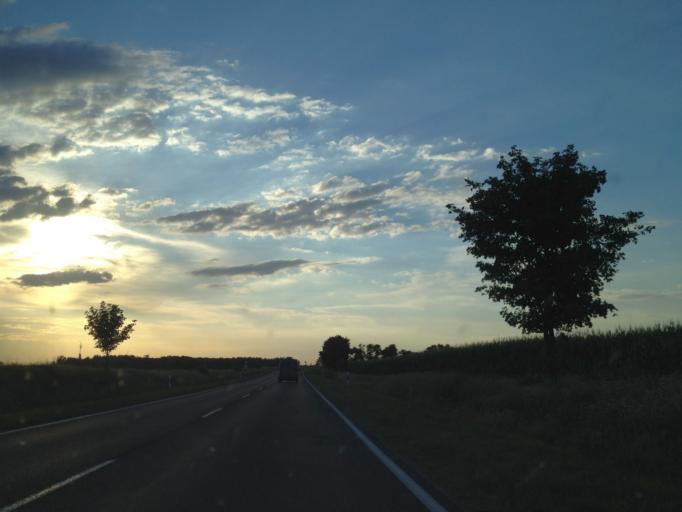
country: HU
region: Gyor-Moson-Sopron
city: Mosonszentmiklos
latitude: 47.7477
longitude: 17.4572
